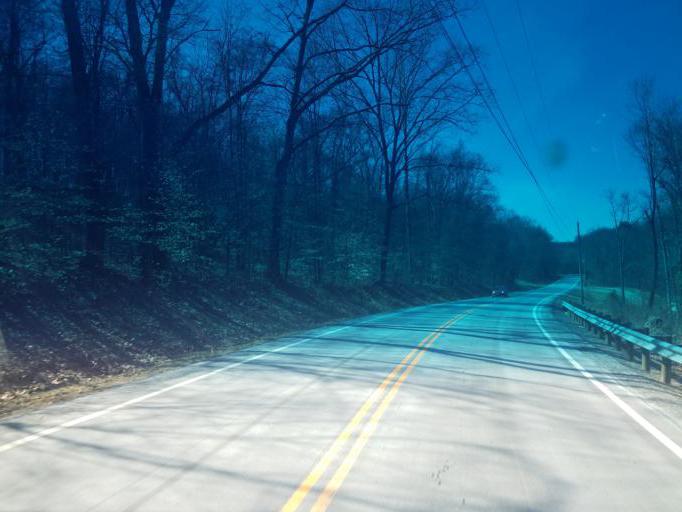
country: US
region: Ohio
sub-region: Knox County
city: Oak Hill
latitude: 40.4630
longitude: -82.1350
